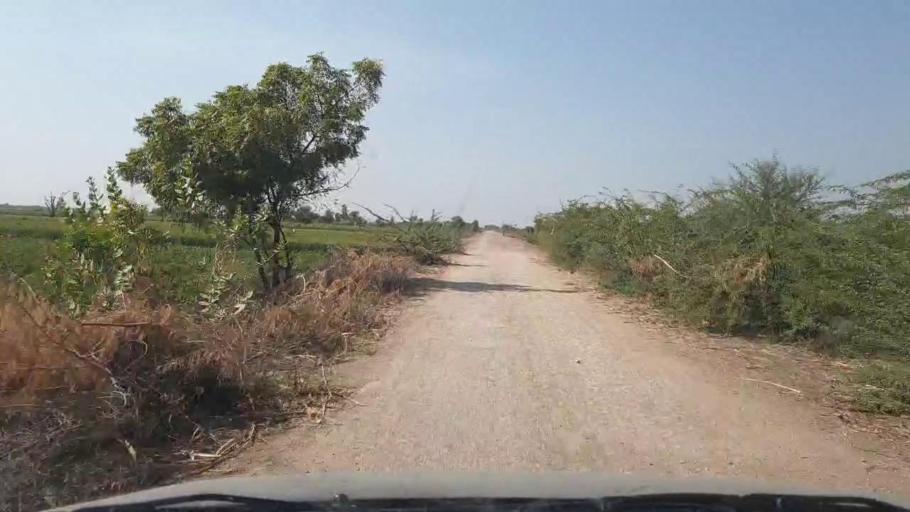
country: PK
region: Sindh
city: Samaro
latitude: 25.1918
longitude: 69.3500
